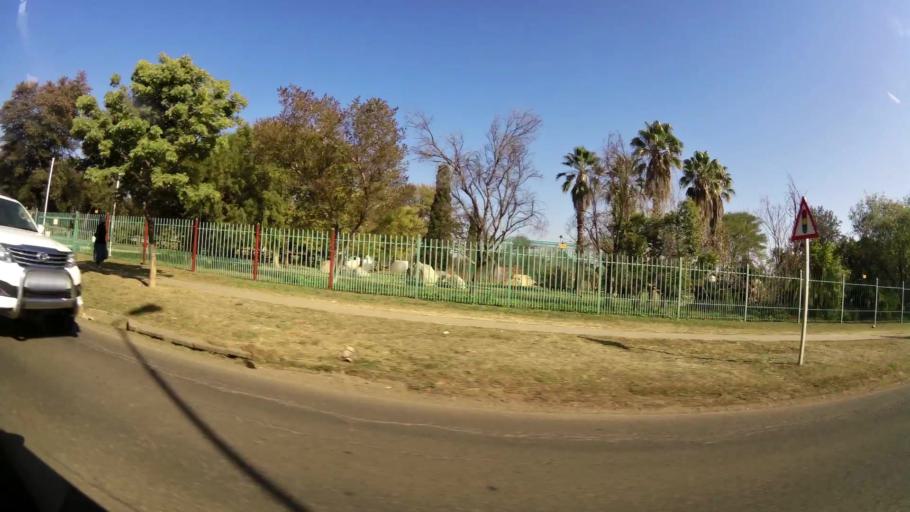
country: ZA
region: Gauteng
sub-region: City of Tshwane Metropolitan Municipality
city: Pretoria
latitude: -25.6614
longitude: 28.2440
